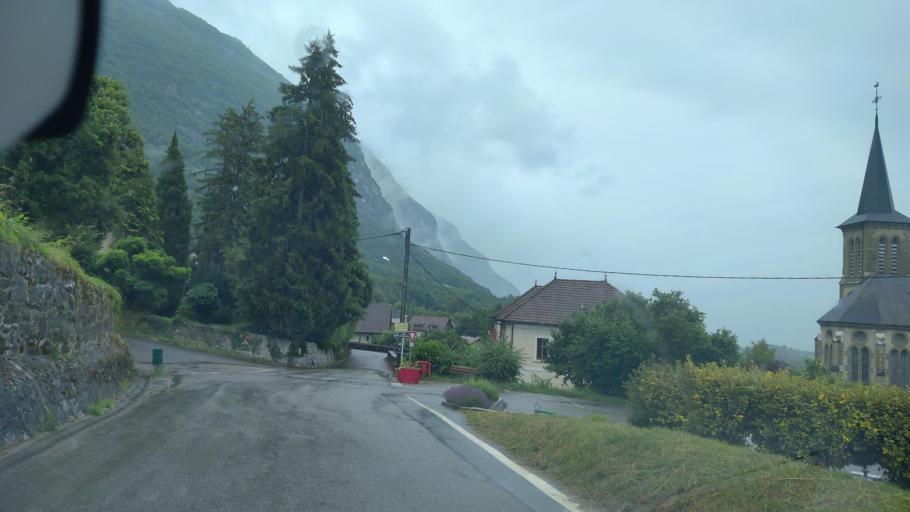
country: FR
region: Rhone-Alpes
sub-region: Departement de la Savoie
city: Chindrieux
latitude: 45.8223
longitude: 5.8513
